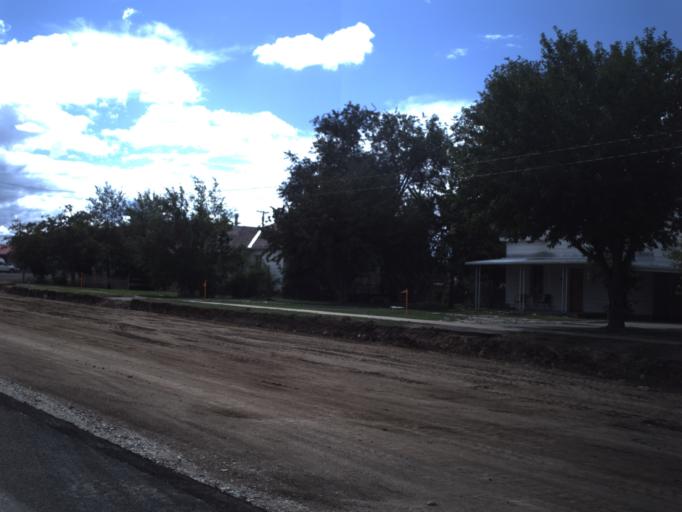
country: US
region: Utah
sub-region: Millard County
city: Fillmore
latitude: 38.9726
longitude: -112.3237
